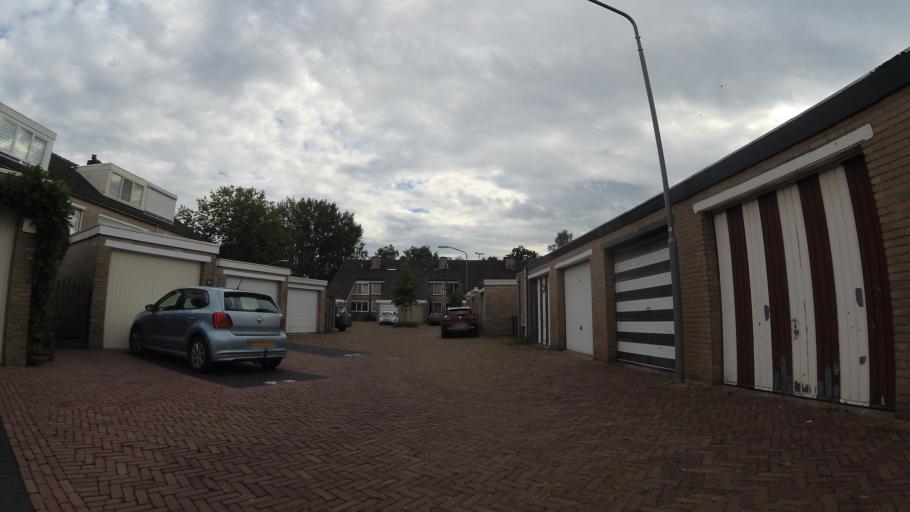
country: NL
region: North Brabant
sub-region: Gemeente Made en Drimmelen
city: Made
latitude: 51.6704
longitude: 4.7874
